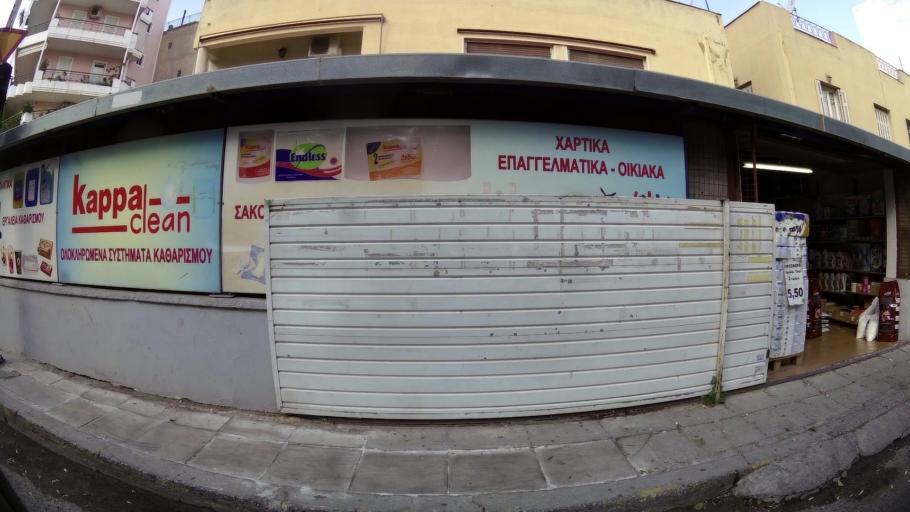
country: GR
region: Attica
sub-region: Nomarchia Athinas
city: Kipseli
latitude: 38.0097
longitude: 23.7389
